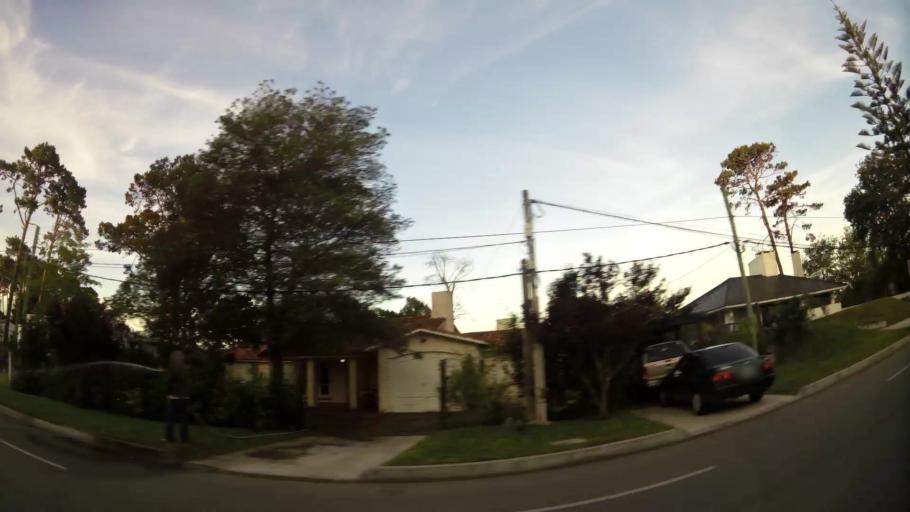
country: UY
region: Maldonado
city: Maldonado
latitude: -34.9241
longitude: -54.9429
